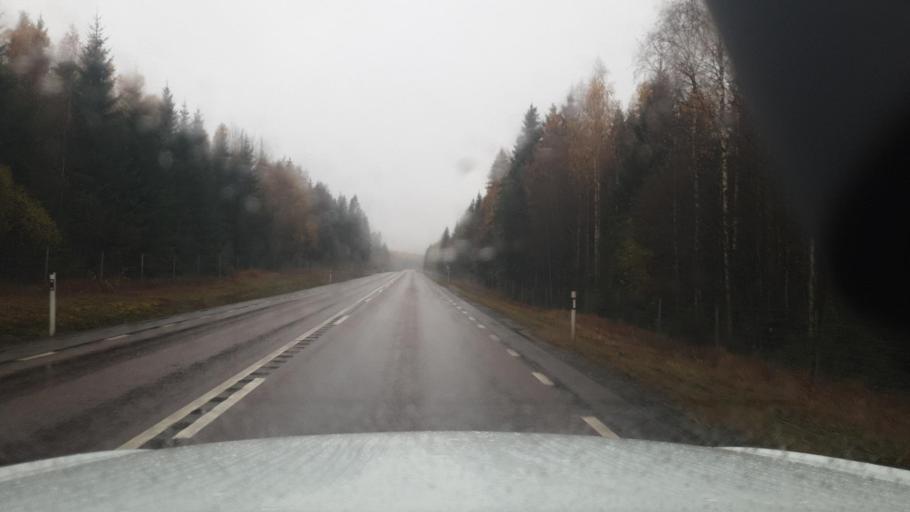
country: SE
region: Vaermland
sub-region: Sunne Kommun
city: Sunne
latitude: 59.7654
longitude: 13.1088
